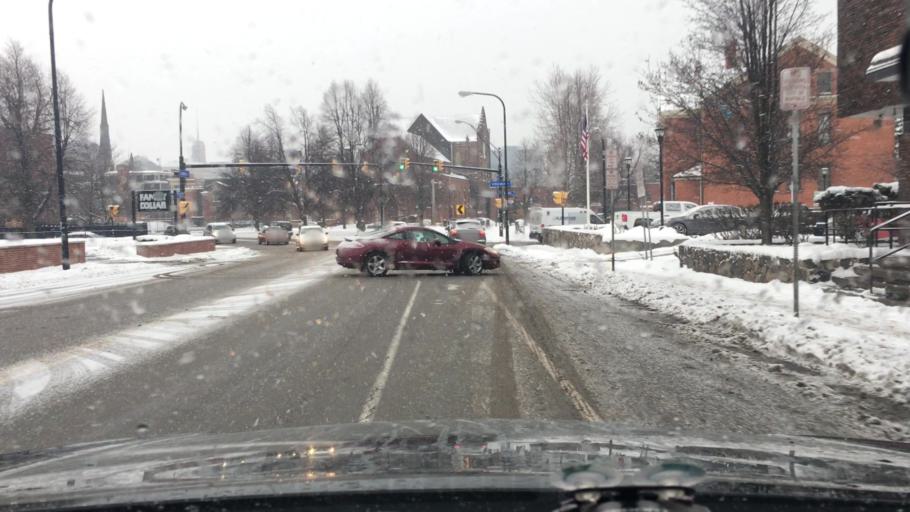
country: US
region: New York
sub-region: Erie County
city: Buffalo
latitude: 42.8975
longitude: -78.8772
